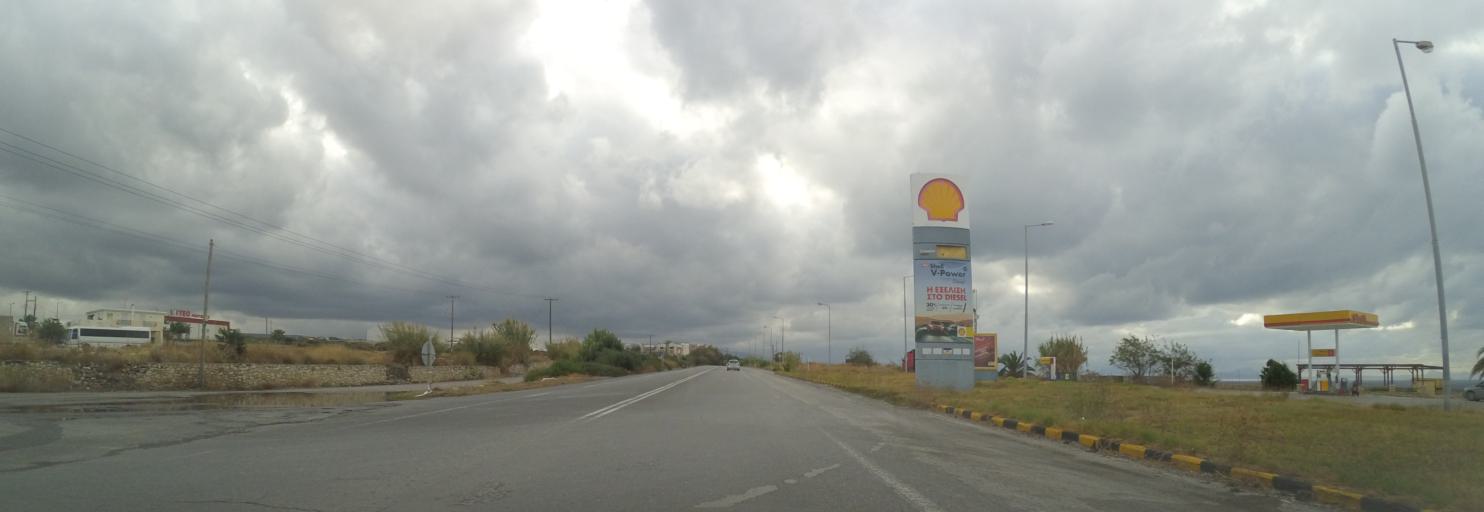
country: GR
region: Crete
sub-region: Nomos Rethymnis
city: Panormos
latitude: 35.4030
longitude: 24.6316
